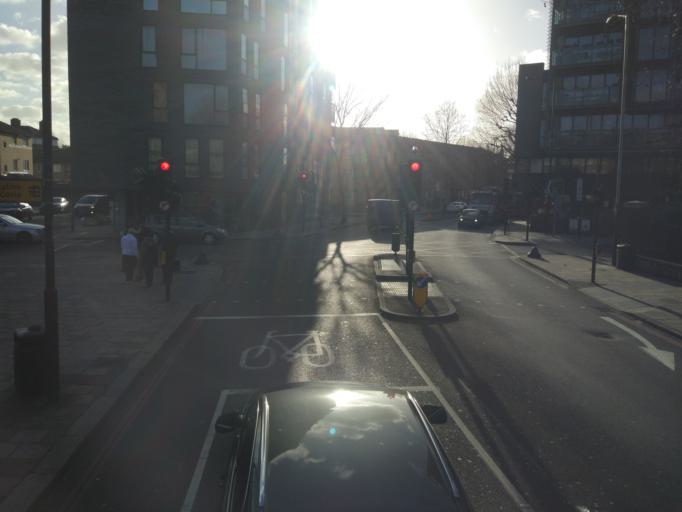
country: GB
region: England
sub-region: Greater London
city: City of London
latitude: 51.4979
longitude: -0.0795
